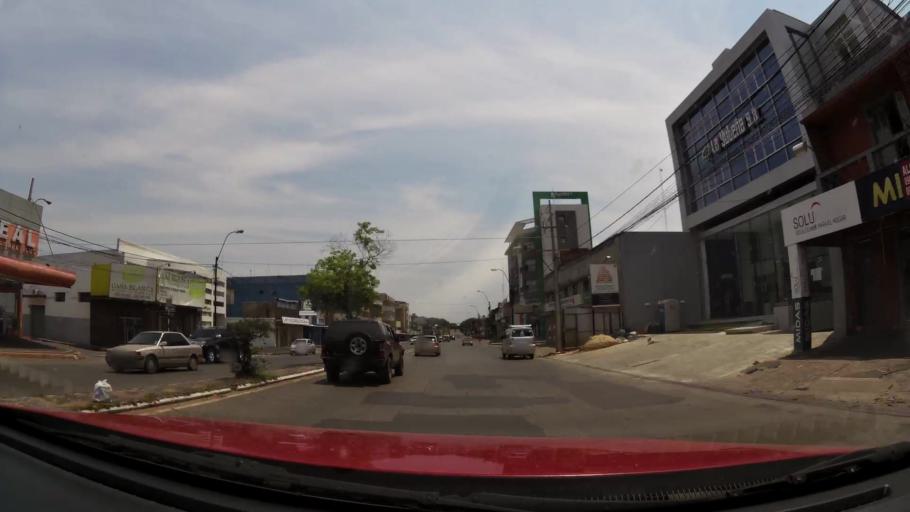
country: PY
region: Asuncion
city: Asuncion
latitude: -25.3039
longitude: -57.6106
